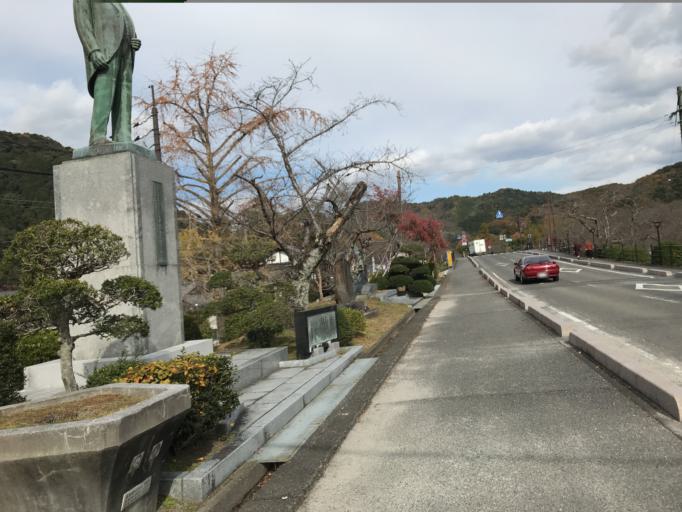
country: JP
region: Yamaguchi
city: Iwakuni
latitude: 34.1693
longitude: 132.1782
